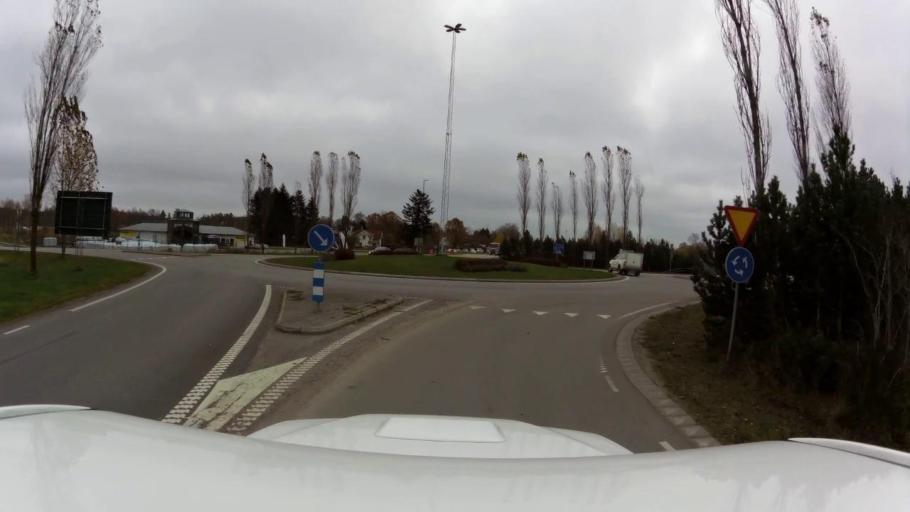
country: SE
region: OEstergoetland
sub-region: Kinda Kommun
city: Rimforsa
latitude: 58.1393
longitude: 15.6800
